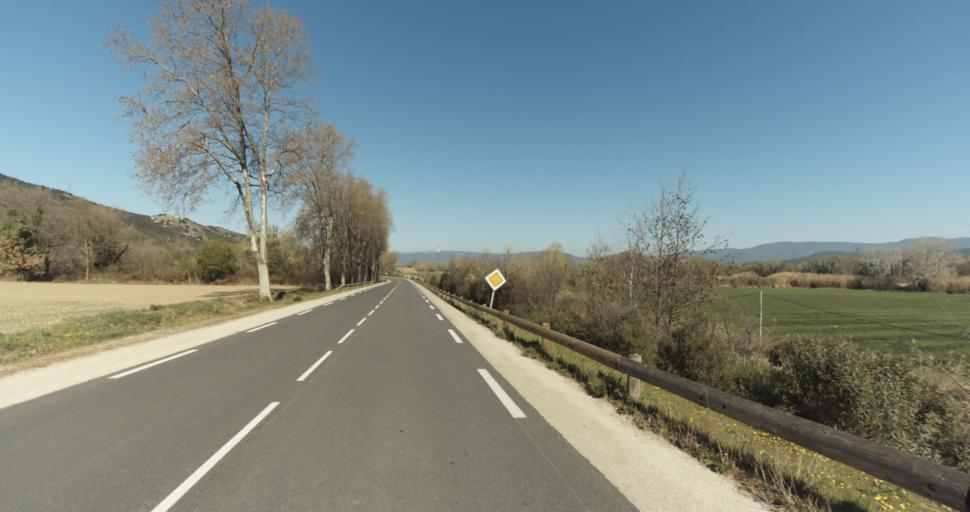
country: FR
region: Provence-Alpes-Cote d'Azur
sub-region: Departement du Vaucluse
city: Villelaure
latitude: 43.6896
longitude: 5.3936
